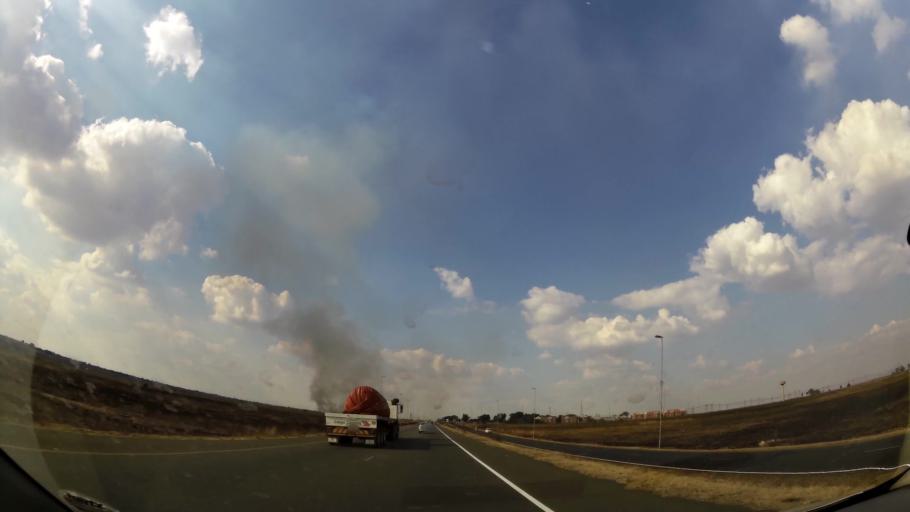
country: ZA
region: Gauteng
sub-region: Ekurhuleni Metropolitan Municipality
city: Boksburg
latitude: -26.2778
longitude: 28.2661
